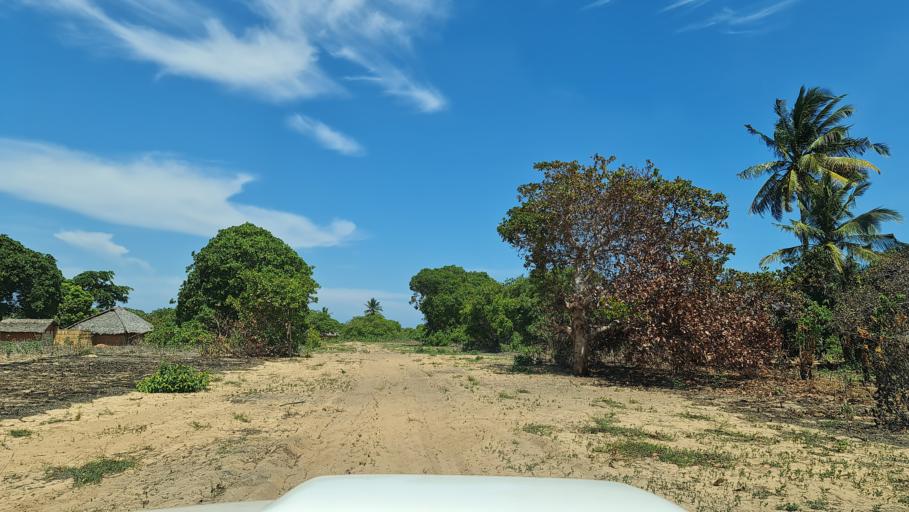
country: MZ
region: Nampula
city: Ilha de Mocambique
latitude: -15.1984
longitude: 40.6107
